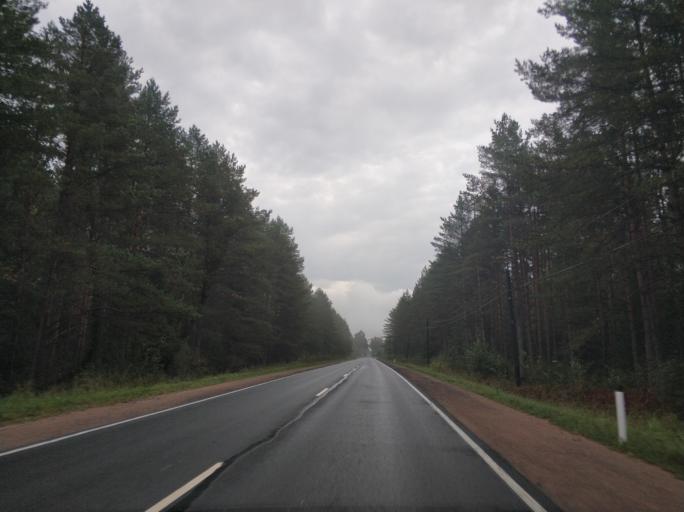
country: RU
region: Leningrad
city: Borisova Griva
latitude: 60.0877
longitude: 30.8705
